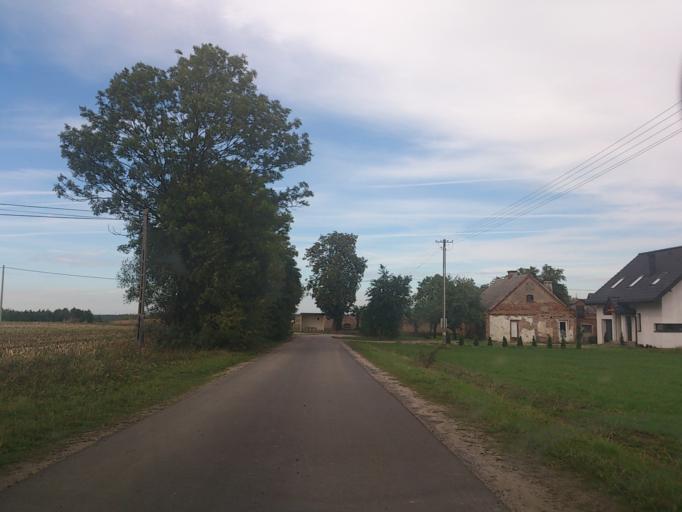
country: PL
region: Kujawsko-Pomorskie
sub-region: Powiat golubsko-dobrzynski
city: Radomin
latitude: 53.1211
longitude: 19.1368
